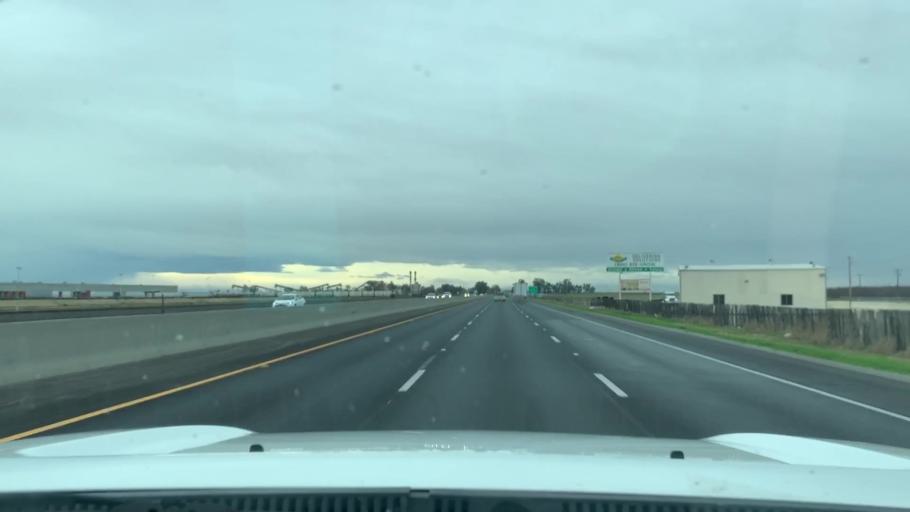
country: US
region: California
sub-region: Kern County
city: Delano
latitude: 35.7317
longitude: -119.2399
